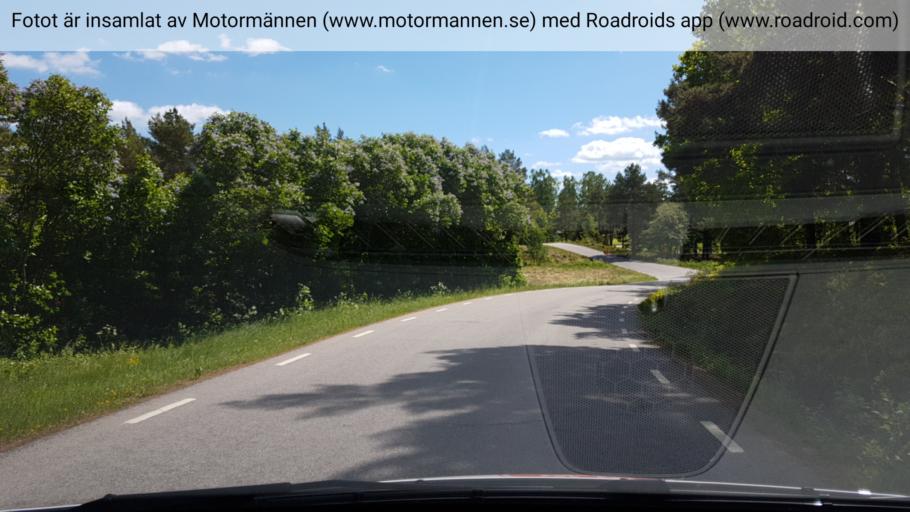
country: SE
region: Kalmar
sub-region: Vasterviks Kommun
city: Vaestervik
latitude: 57.9157
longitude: 16.6906
